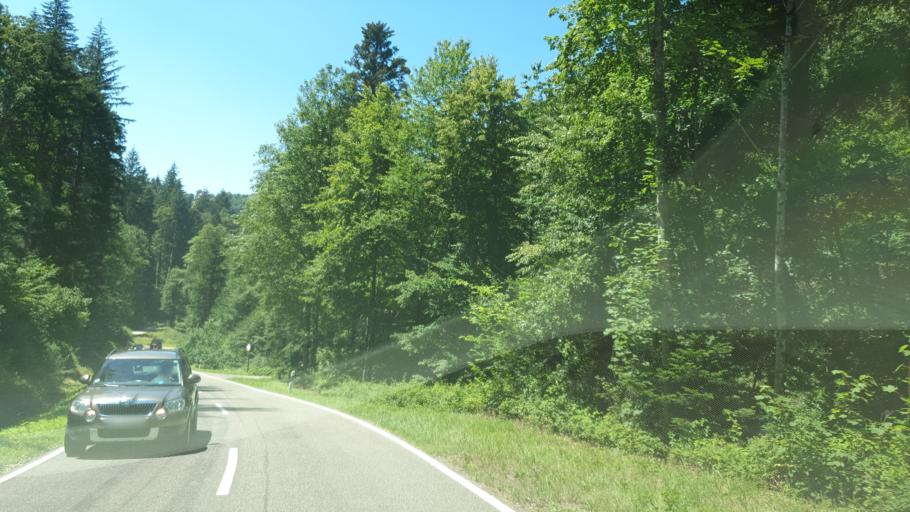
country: DE
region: Baden-Wuerttemberg
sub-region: Freiburg Region
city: Horben
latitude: 47.9402
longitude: 7.8743
